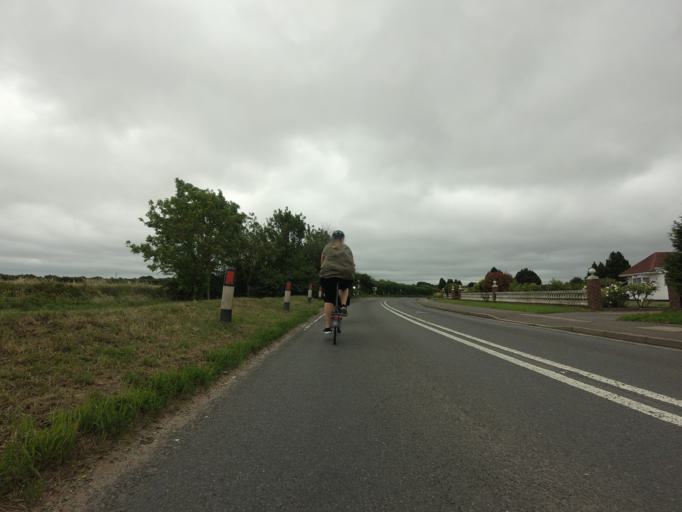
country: GB
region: England
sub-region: Kent
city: Longfield
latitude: 51.4108
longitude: 0.2820
